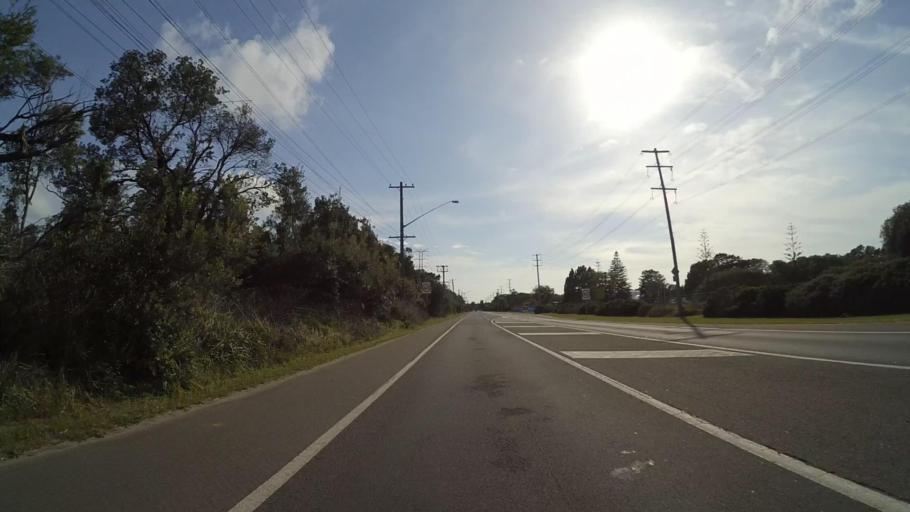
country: AU
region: New South Wales
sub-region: Sutherland Shire
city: Kurnell
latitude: -34.0219
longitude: 151.1976
